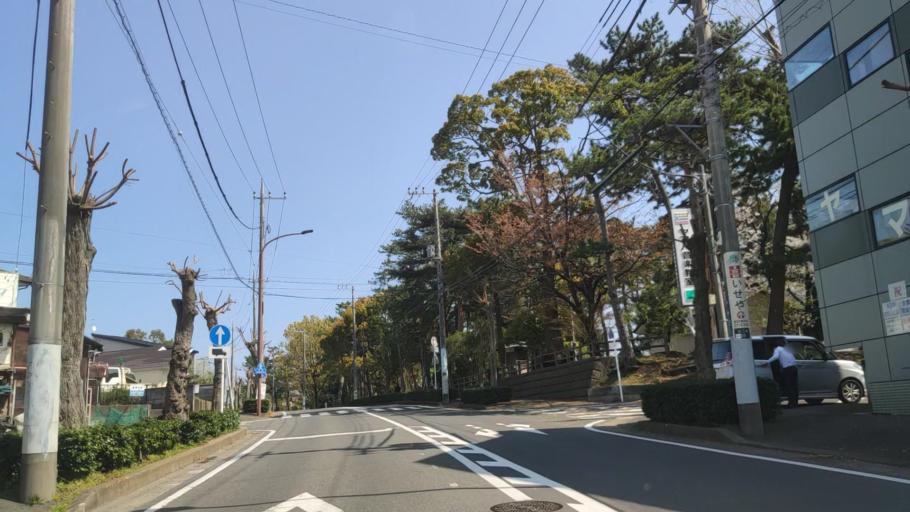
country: JP
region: Kanagawa
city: Hiratsuka
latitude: 35.3331
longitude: 139.3266
